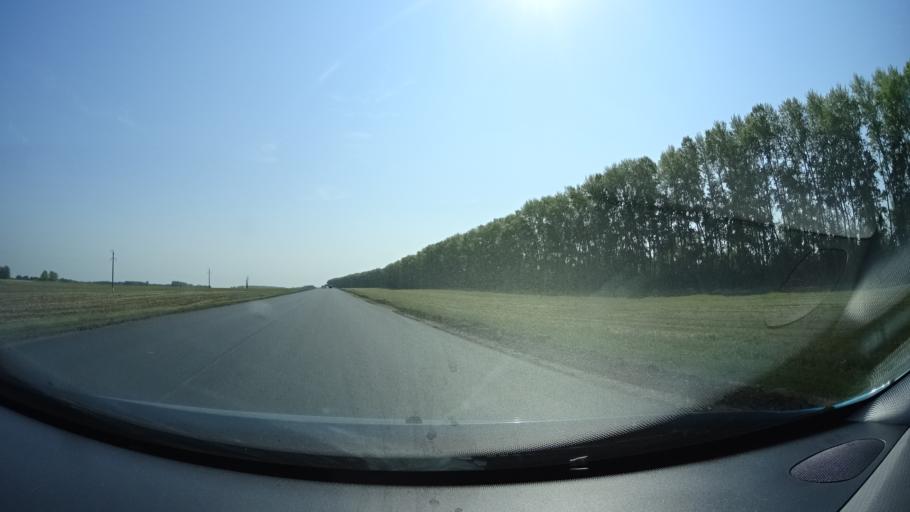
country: RU
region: Bashkortostan
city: Karmaskaly
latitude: 54.4071
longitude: 56.0752
